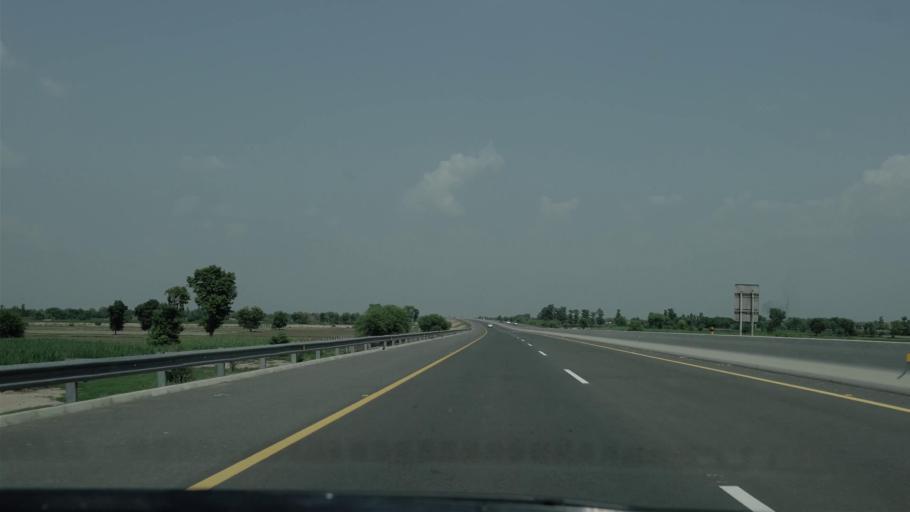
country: PK
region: Punjab
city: Gojra
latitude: 31.1914
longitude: 72.6500
